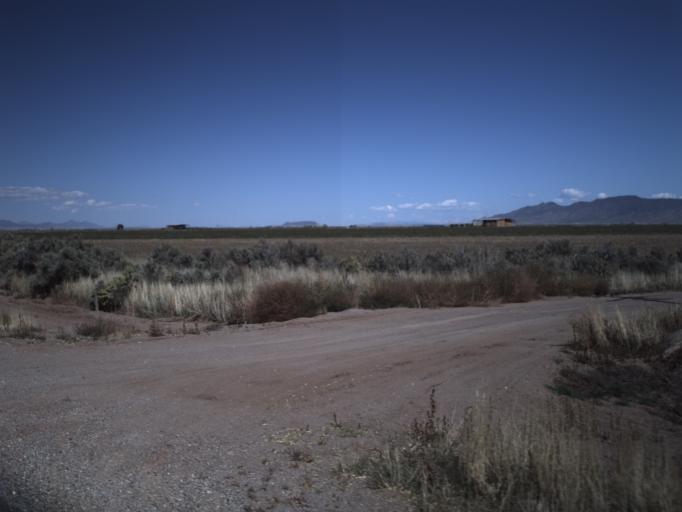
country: US
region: Utah
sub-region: Washington County
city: Enterprise
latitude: 37.6192
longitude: -113.6612
